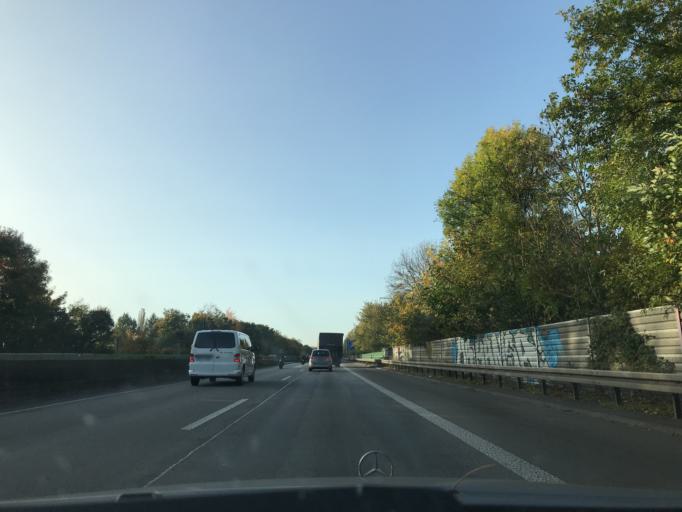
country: DE
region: North Rhine-Westphalia
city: Castrop-Rauxel
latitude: 51.5736
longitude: 7.3636
